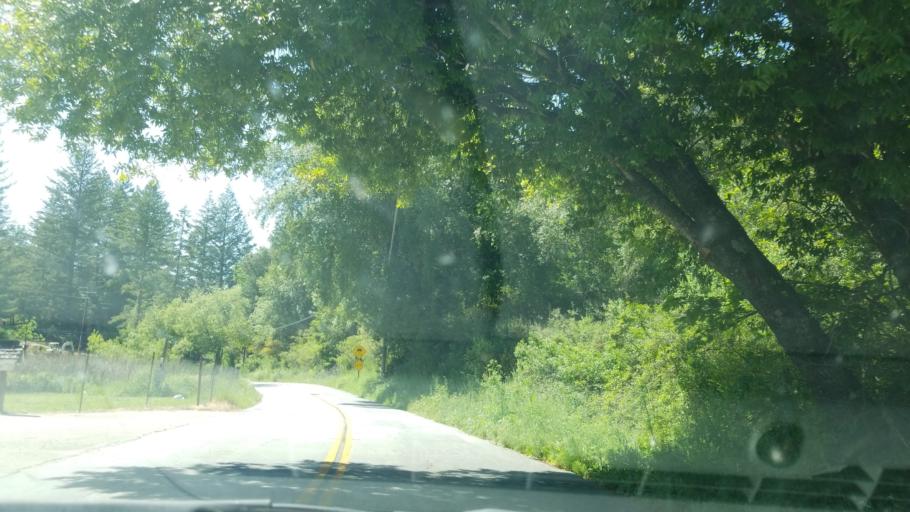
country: US
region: California
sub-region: Santa Cruz County
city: Day Valley
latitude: 37.1079
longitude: -121.9033
